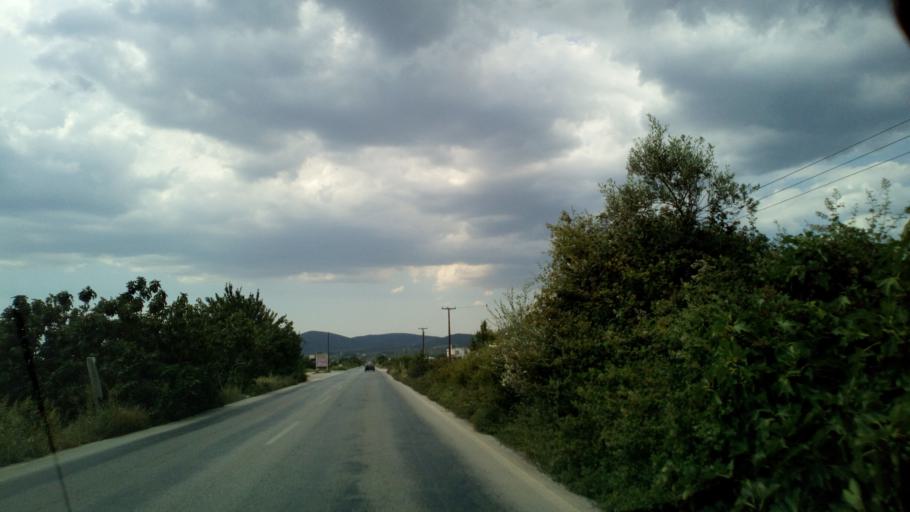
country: GR
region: Central Macedonia
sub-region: Nomos Chalkidikis
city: Ormylia
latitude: 40.2569
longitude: 23.5360
